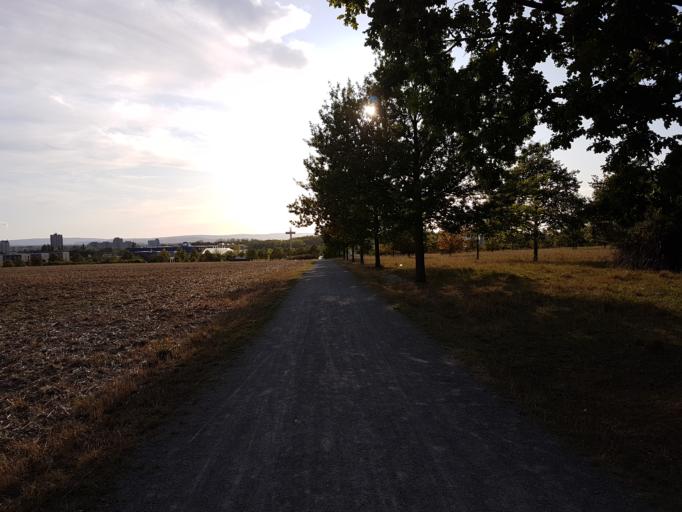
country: DE
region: Lower Saxony
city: Laatzen
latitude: 52.3174
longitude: 9.8271
